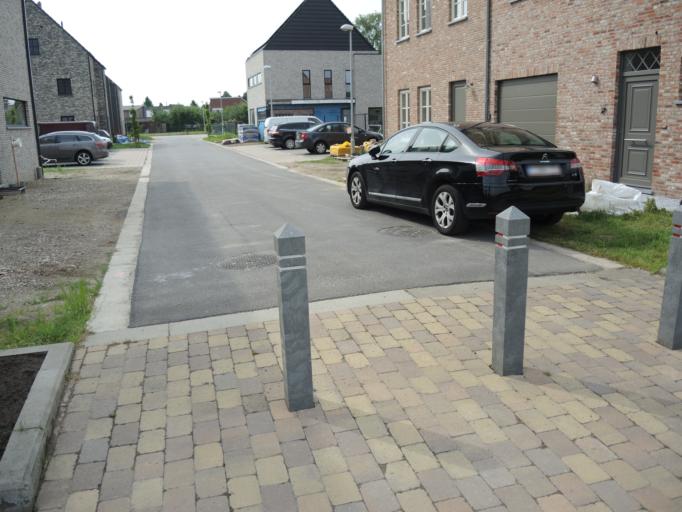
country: BE
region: Flanders
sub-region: Provincie Antwerpen
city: Oud-Turnhout
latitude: 51.3093
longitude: 4.9946
